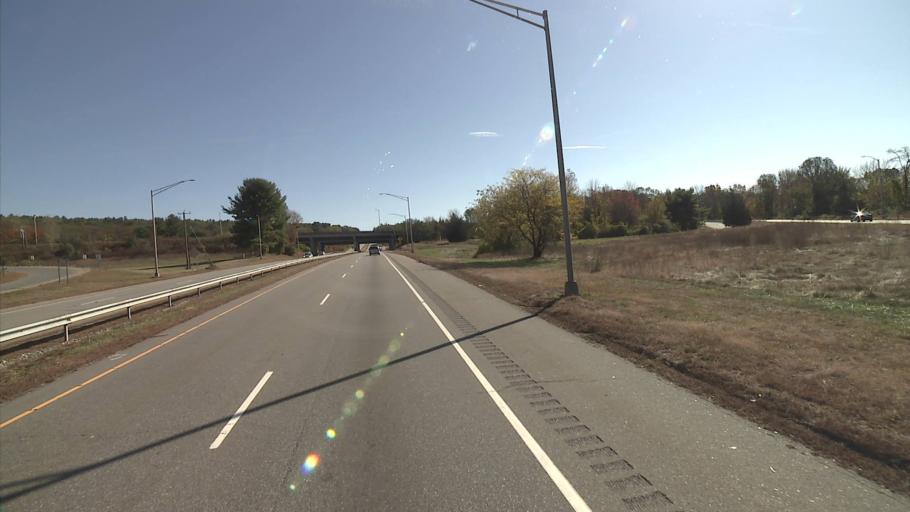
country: US
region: Connecticut
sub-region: Windham County
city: Danielson
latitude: 41.7941
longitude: -71.8793
